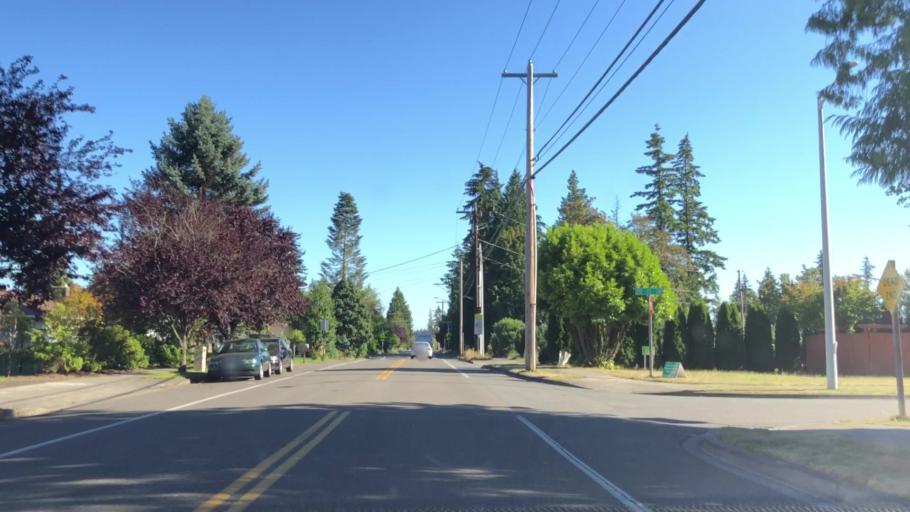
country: US
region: Washington
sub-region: Snohomish County
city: Martha Lake
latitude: 47.8602
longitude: -122.2578
